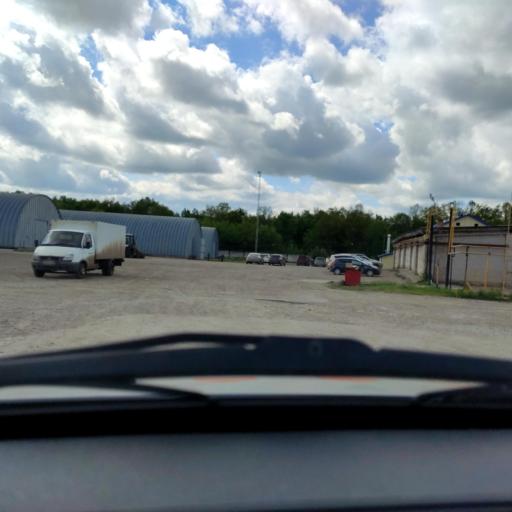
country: RU
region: Bashkortostan
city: Mikhaylovka
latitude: 54.8036
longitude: 55.8506
